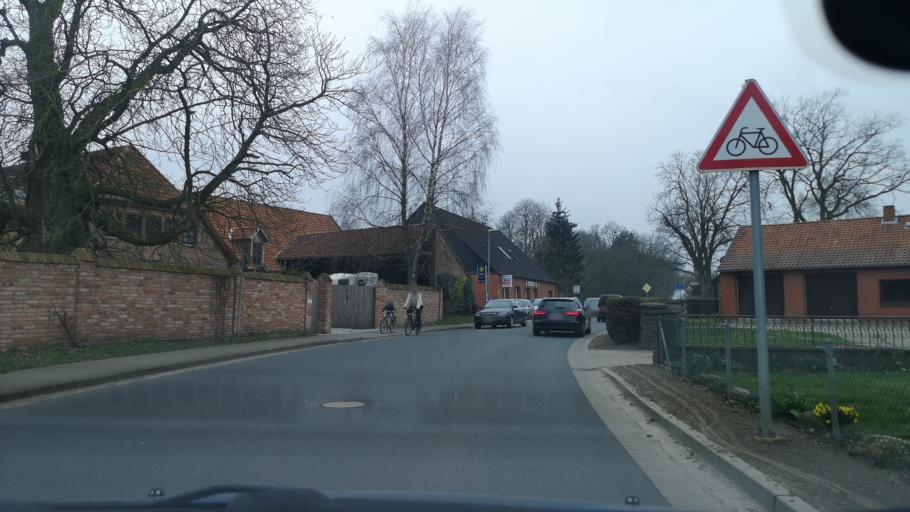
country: DE
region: Lower Saxony
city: Neustadt am Rubenberge
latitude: 52.5707
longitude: 9.4978
